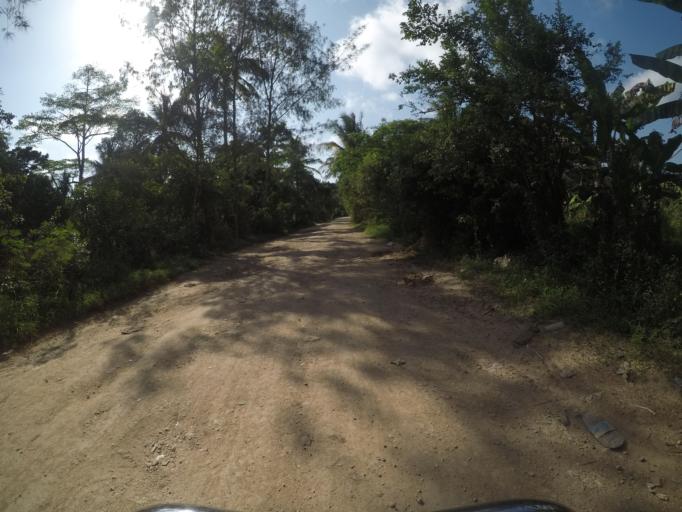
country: TZ
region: Zanzibar Central/South
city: Koani
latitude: -6.2188
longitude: 39.3264
